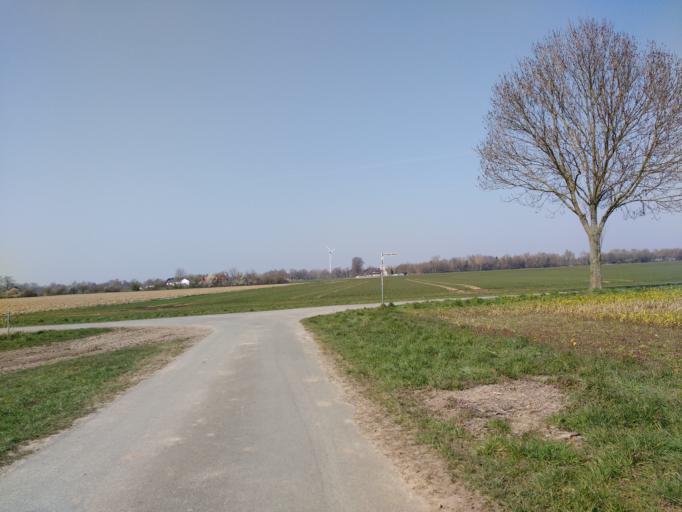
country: DE
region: North Rhine-Westphalia
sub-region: Regierungsbezirk Detmold
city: Salzkotten
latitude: 51.7296
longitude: 8.6466
